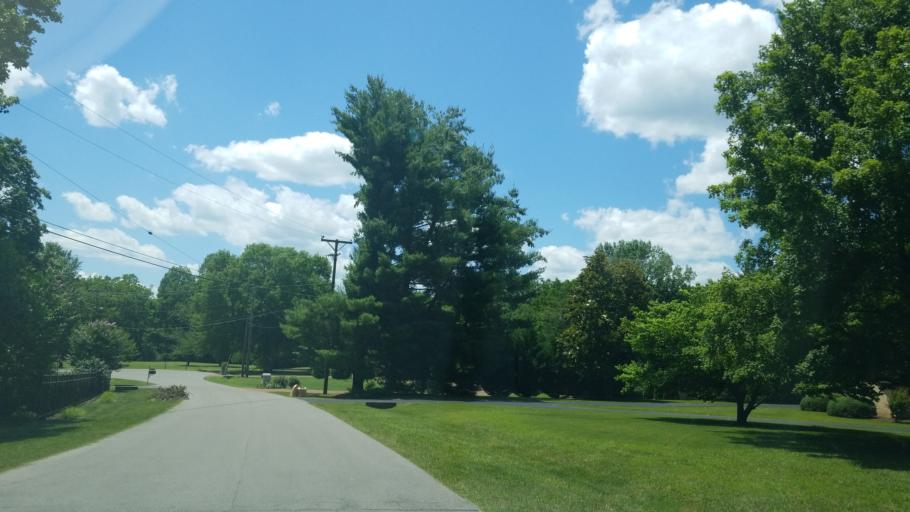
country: US
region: Tennessee
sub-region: Davidson County
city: Forest Hills
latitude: 36.0329
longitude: -86.8285
